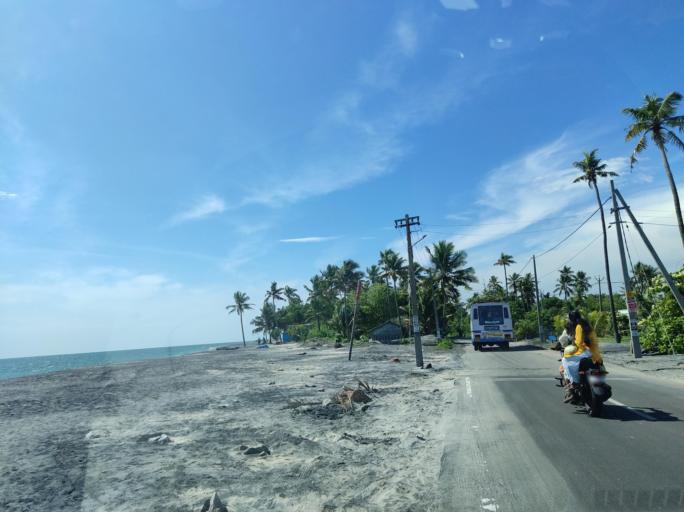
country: IN
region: Kerala
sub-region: Alappuzha
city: Kayankulam
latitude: 9.1674
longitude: 76.4492
